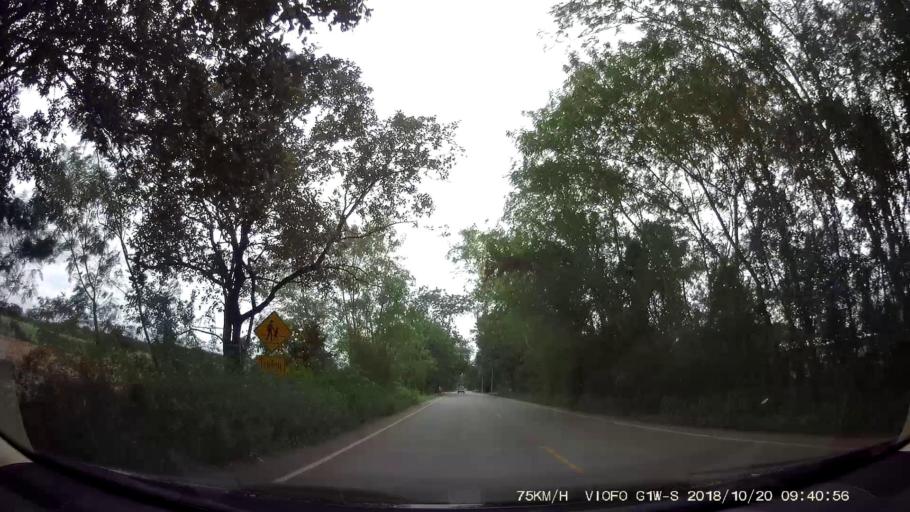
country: TH
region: Chaiyaphum
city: Kaset Sombun
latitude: 16.4479
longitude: 101.9593
